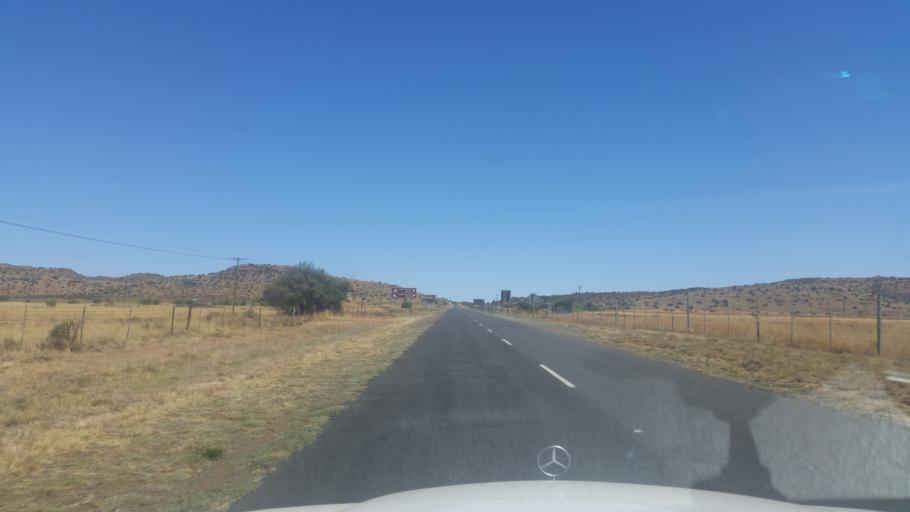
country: ZA
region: Eastern Cape
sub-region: Joe Gqabi District Municipality
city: Burgersdorp
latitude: -30.7802
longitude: 25.7635
